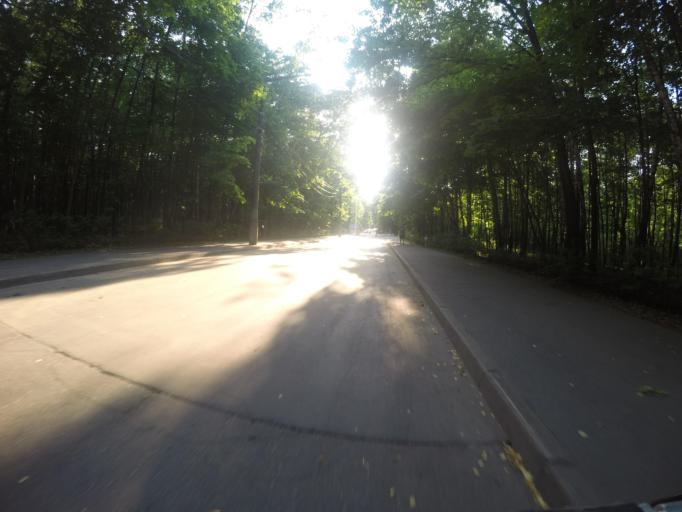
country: RU
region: Moscow
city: Sokol'niki
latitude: 55.7974
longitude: 37.6591
